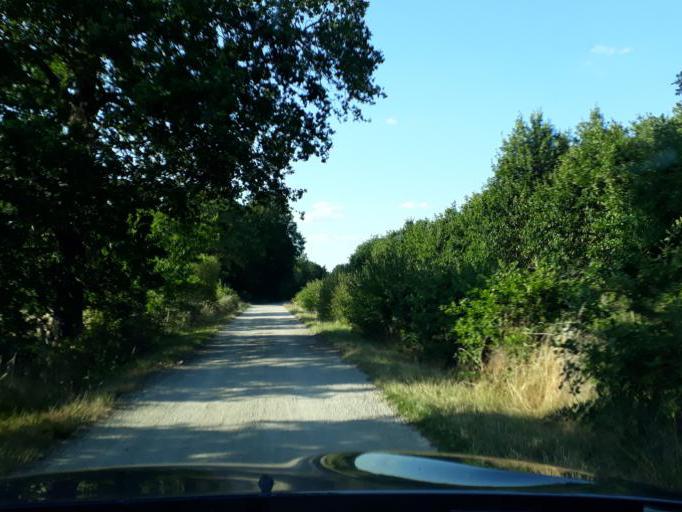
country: FR
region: Centre
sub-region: Departement du Loiret
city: Chaingy
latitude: 47.8969
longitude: 1.7407
